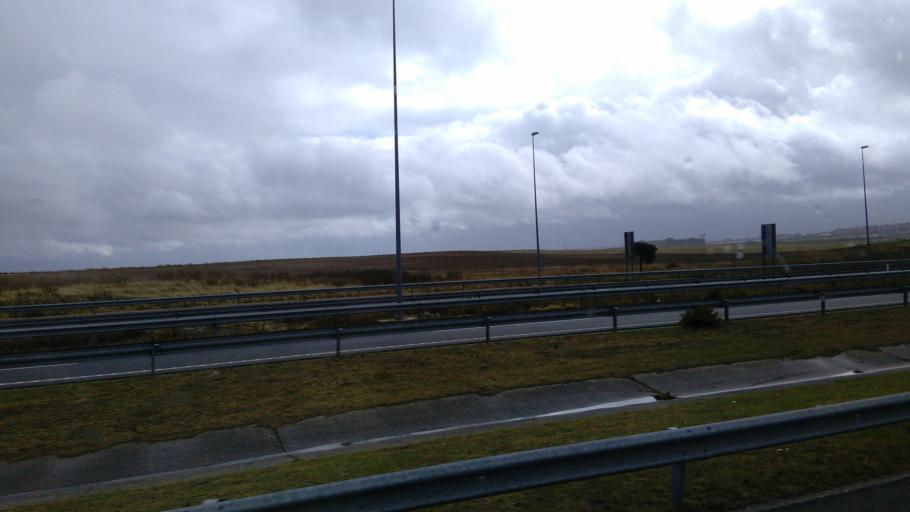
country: ES
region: Madrid
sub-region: Provincia de Madrid
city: Alcorcon
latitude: 40.3254
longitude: -3.8173
